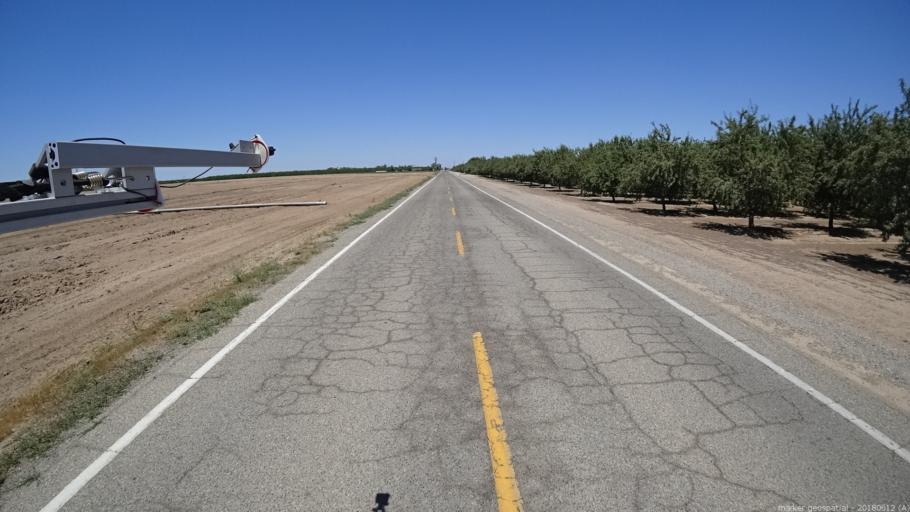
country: US
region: California
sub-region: Madera County
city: Chowchilla
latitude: 37.0753
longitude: -120.2568
